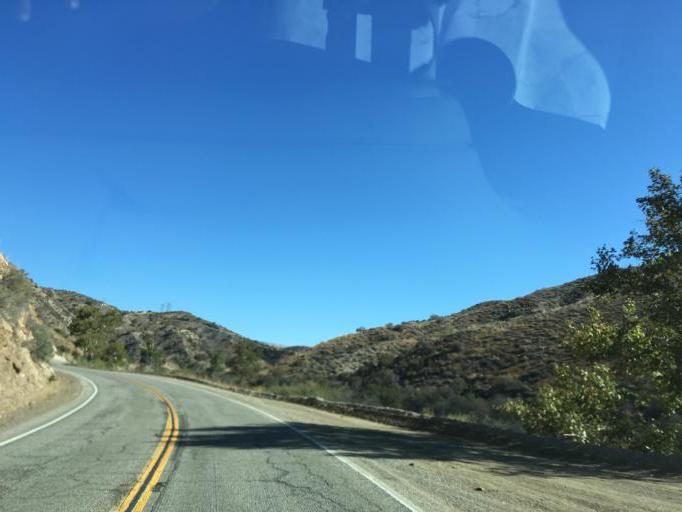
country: US
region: California
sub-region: Los Angeles County
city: Agua Dulce
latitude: 34.4507
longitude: -118.3331
